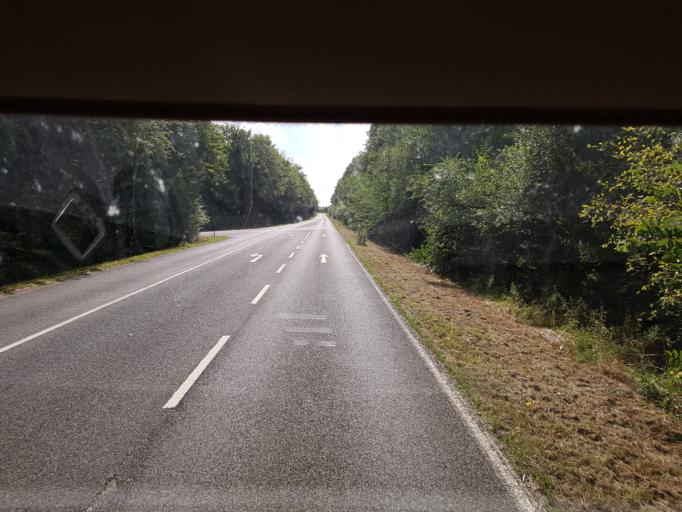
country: DE
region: Rheinland-Pfalz
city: Fohren
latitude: 49.8642
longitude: 6.7810
